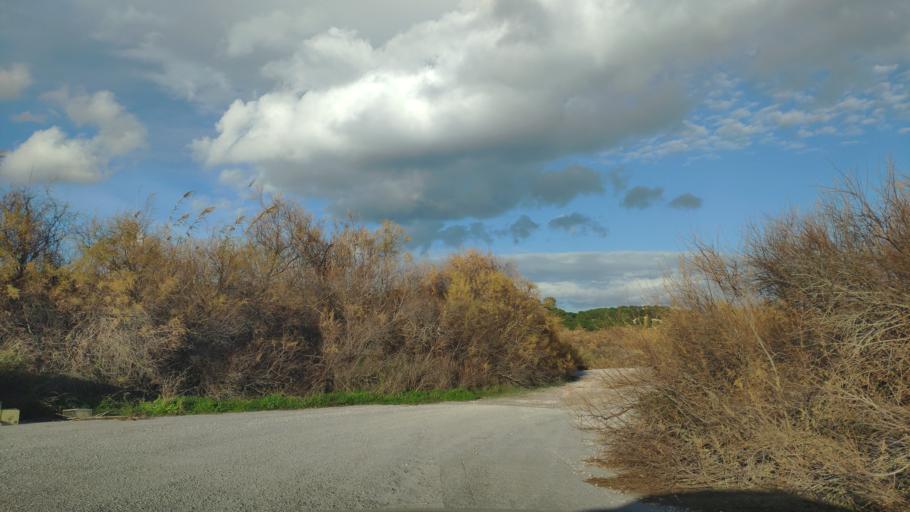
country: GR
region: Attica
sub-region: Nomarchia Anatolikis Attikis
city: Limin Mesoyaias
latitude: 37.9241
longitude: 23.9978
